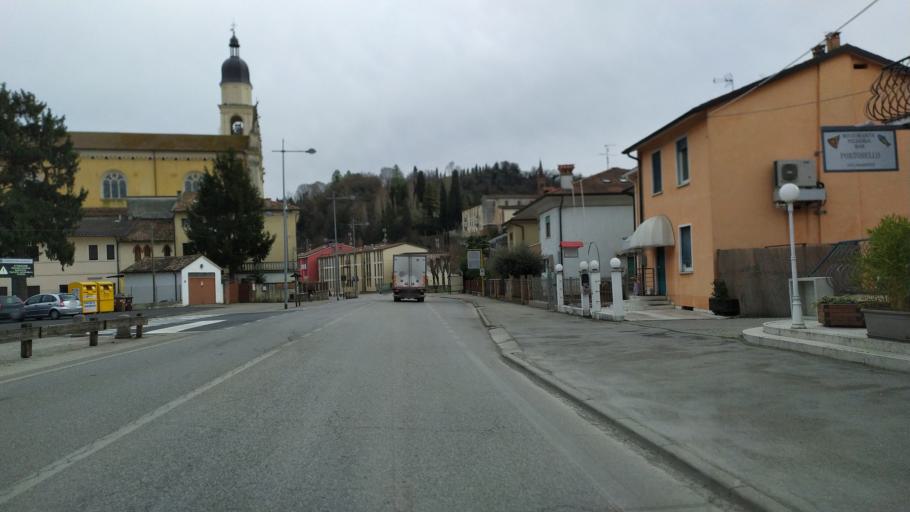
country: IT
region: Veneto
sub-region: Provincia di Vicenza
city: Isola Vicentina
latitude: 45.6309
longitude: 11.4409
